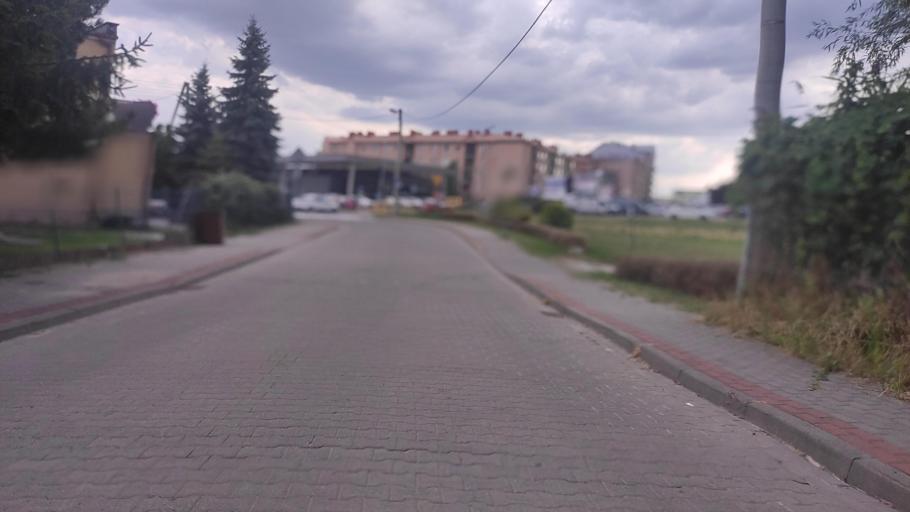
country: PL
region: Greater Poland Voivodeship
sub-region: Powiat poznanski
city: Swarzedz
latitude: 52.4020
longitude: 17.0673
